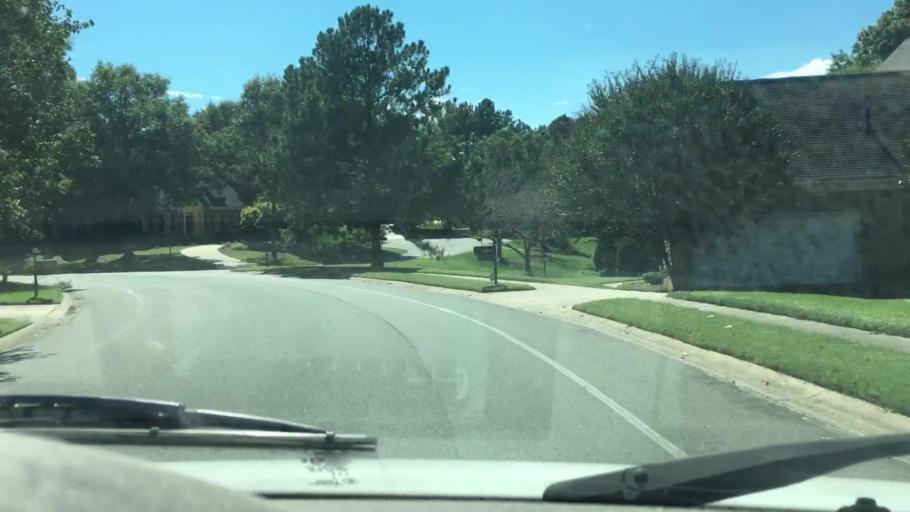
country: US
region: North Carolina
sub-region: Gaston County
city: Davidson
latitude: 35.4668
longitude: -80.8090
